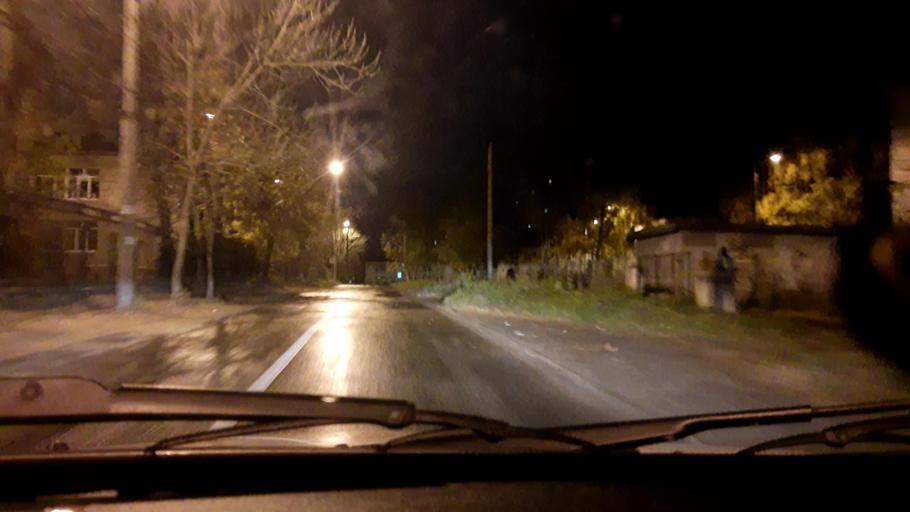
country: RU
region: Bashkortostan
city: Ufa
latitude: 54.8021
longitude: 56.1280
